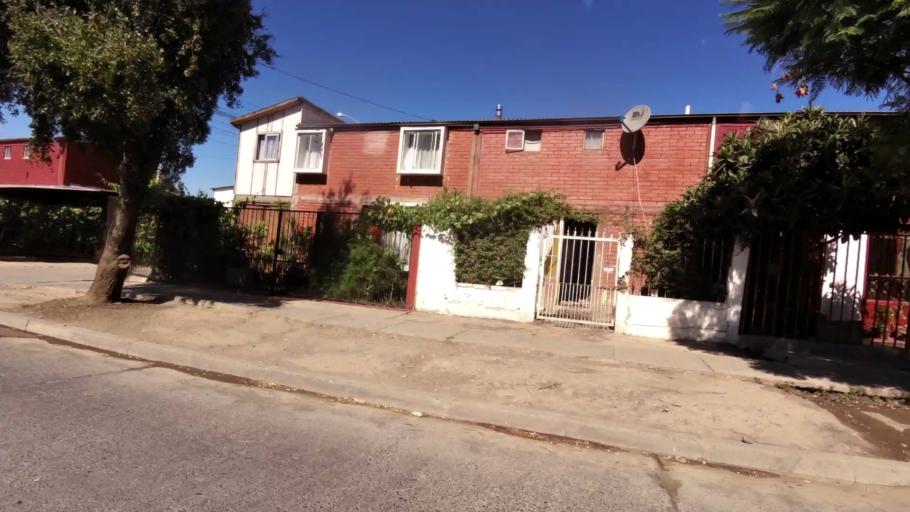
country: CL
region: O'Higgins
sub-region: Provincia de Colchagua
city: Chimbarongo
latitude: -34.5921
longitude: -70.9994
